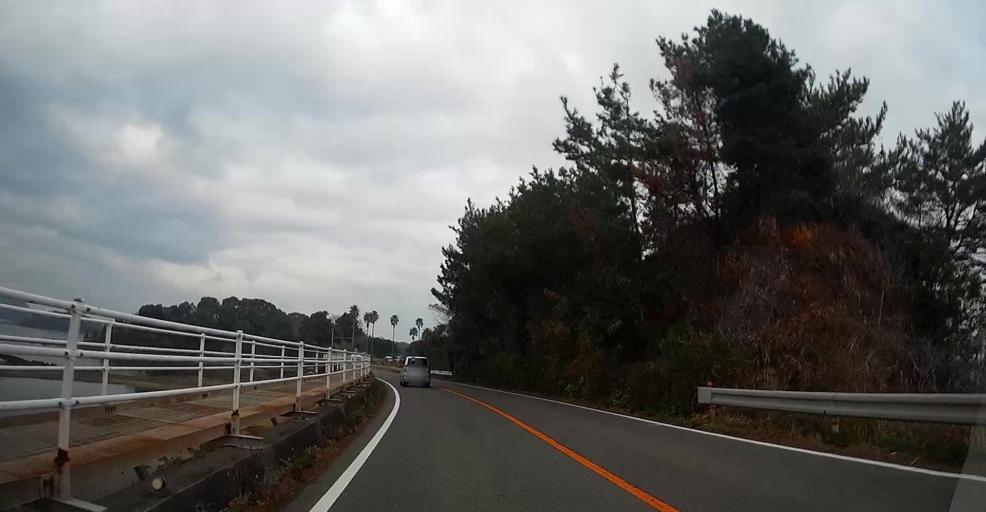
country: JP
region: Kumamoto
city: Yatsushiro
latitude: 32.5335
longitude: 130.4233
